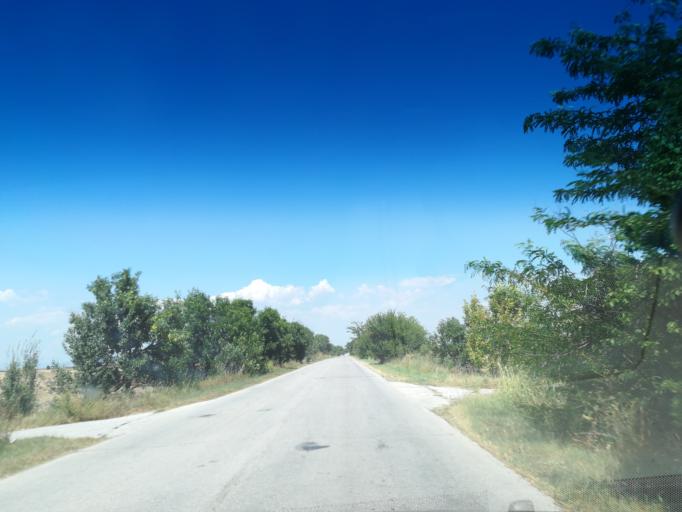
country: BG
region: Plovdiv
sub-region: Obshtina Sadovo
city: Sadovo
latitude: 42.0454
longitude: 25.1393
